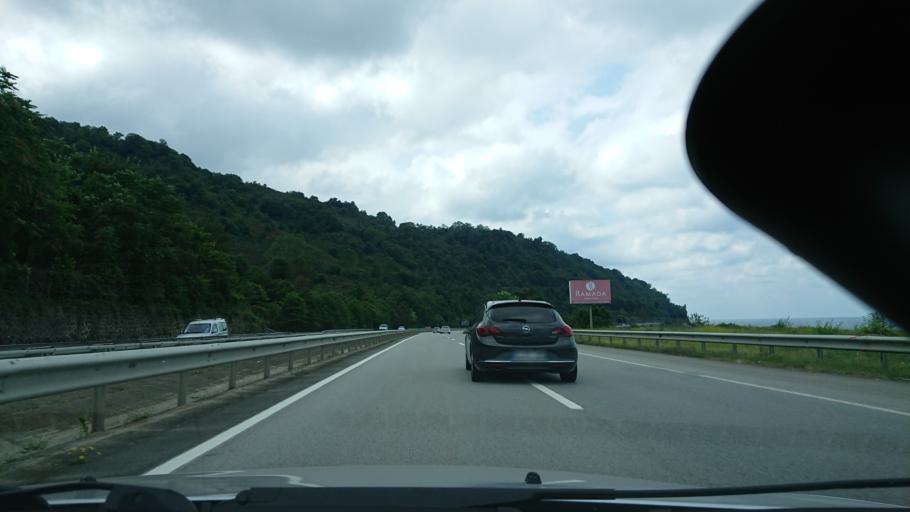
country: TR
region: Giresun
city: Eynesil
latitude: 41.0733
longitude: 39.1794
